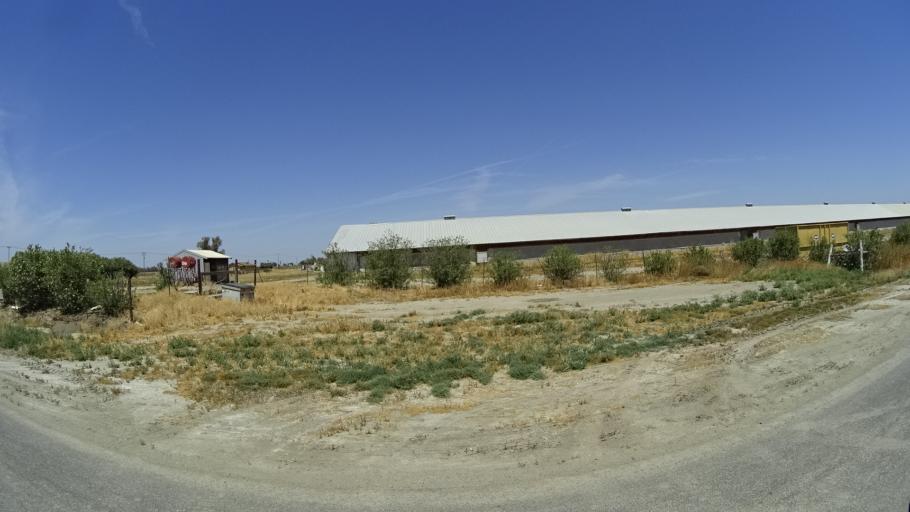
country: US
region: California
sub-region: Kings County
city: Stratford
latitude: 36.2331
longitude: -119.7972
